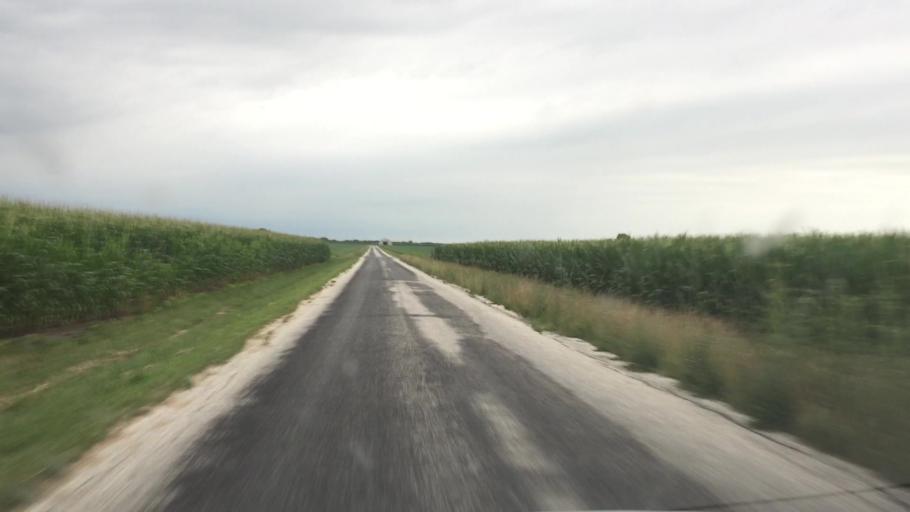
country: US
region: Illinois
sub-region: Adams County
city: Camp Point
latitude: 40.2218
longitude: -90.9691
